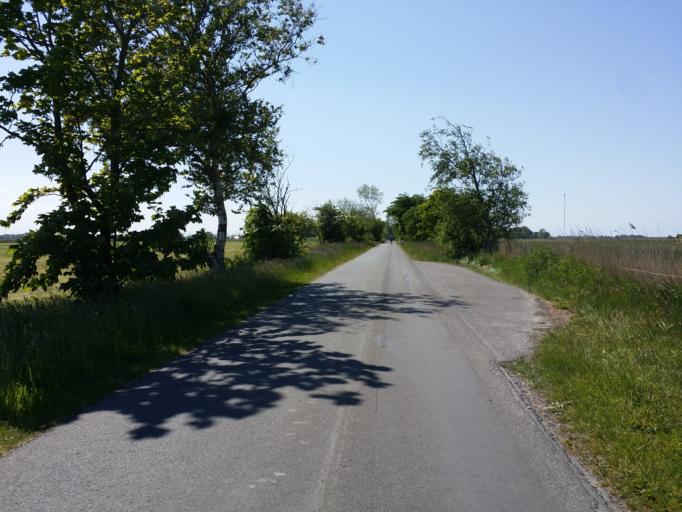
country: DE
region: Lower Saxony
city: Stedesdorf
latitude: 53.6749
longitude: 7.6500
